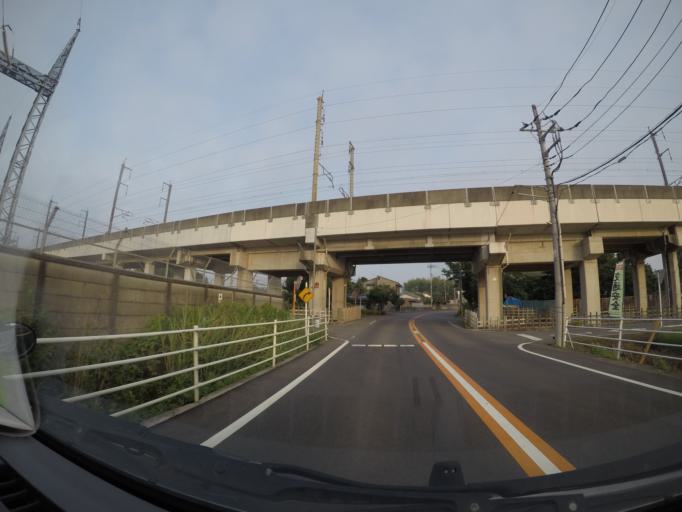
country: JP
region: Ibaraki
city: Koga
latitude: 36.2292
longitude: 139.7589
